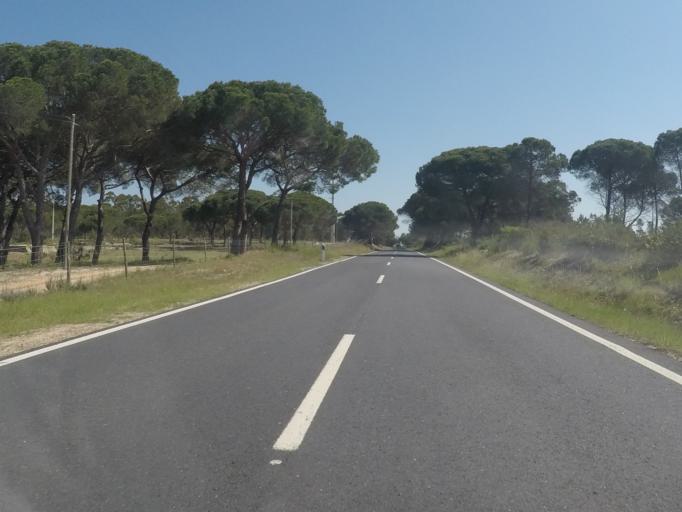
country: PT
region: Setubal
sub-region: Grandola
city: Grandola
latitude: 38.2602
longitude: -8.7332
